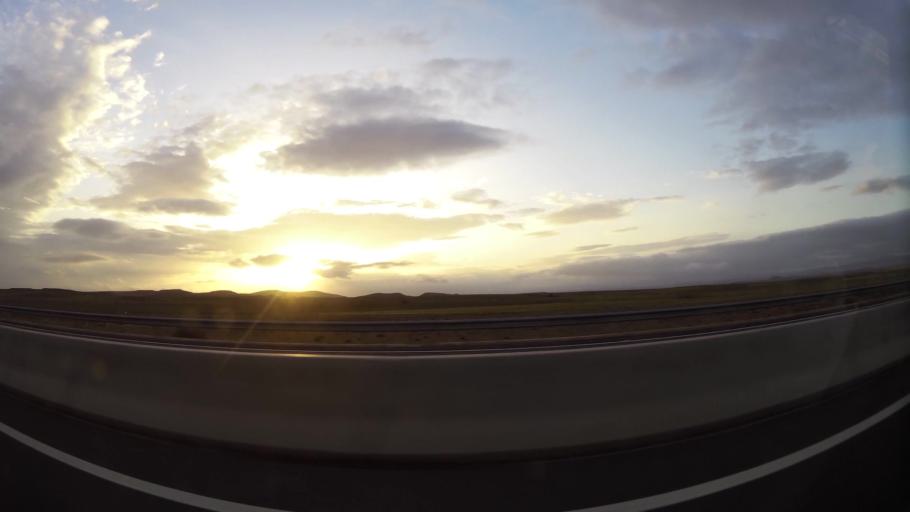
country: MA
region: Oriental
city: Taourirt
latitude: 34.5114
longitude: -2.9436
